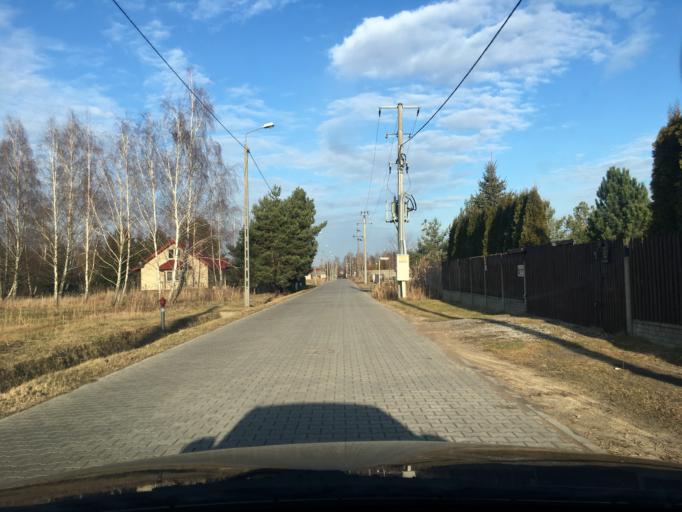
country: PL
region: Masovian Voivodeship
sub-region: Powiat piaseczynski
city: Lesznowola
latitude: 52.0305
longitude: 20.9372
